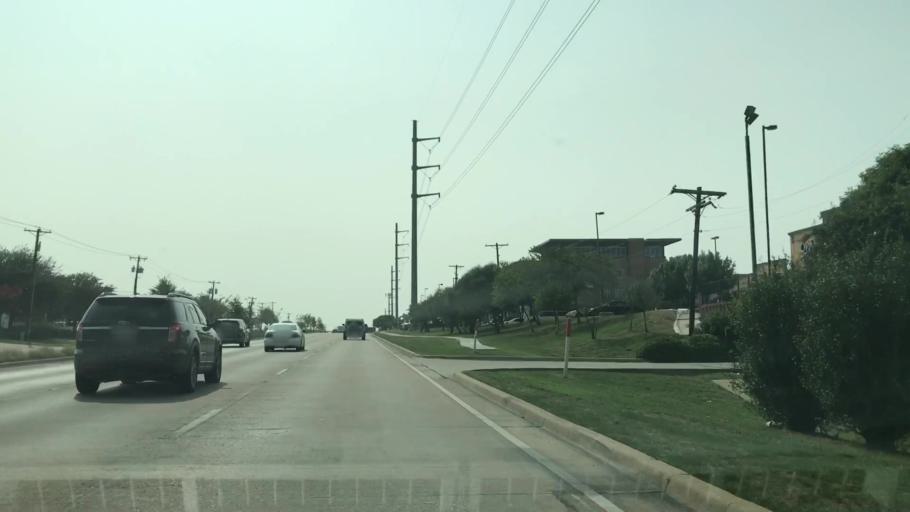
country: US
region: Texas
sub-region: Dallas County
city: Rowlett
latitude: 32.9078
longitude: -96.5639
